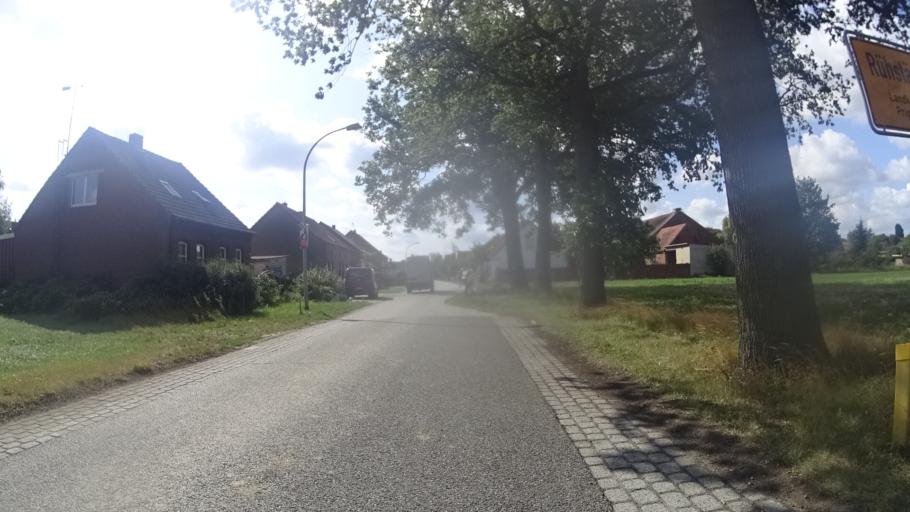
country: DE
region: Brandenburg
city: Ruhstadt
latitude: 52.9231
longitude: 11.8702
